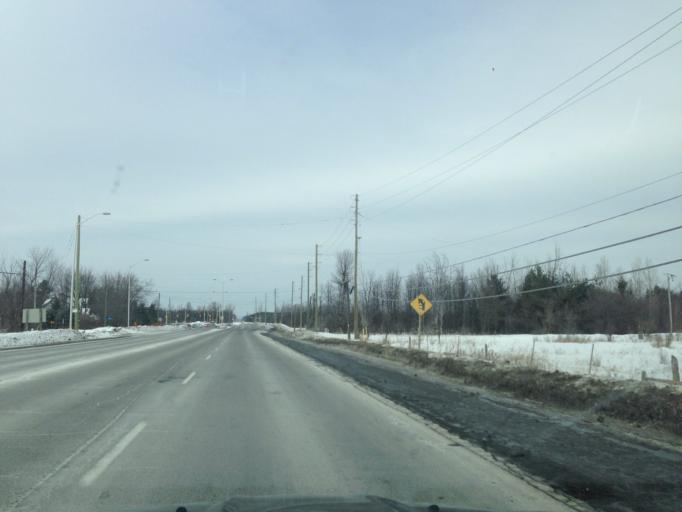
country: CA
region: Ontario
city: Ottawa
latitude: 45.3333
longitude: -75.6011
